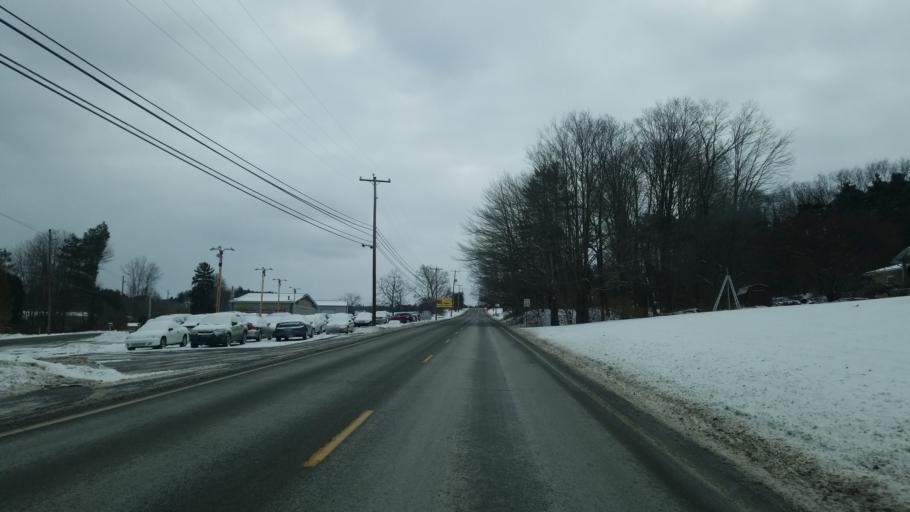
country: US
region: Pennsylvania
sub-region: Clearfield County
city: Sandy
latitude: 41.0839
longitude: -78.7631
